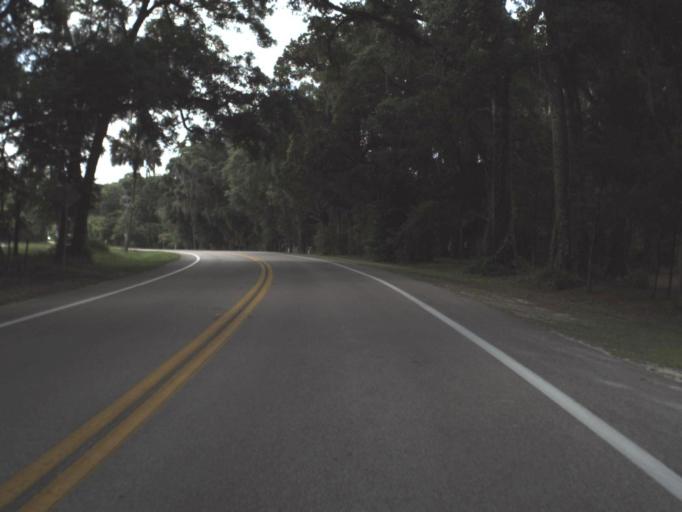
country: US
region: Florida
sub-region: Putnam County
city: East Palatka
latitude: 29.6025
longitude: -81.5834
